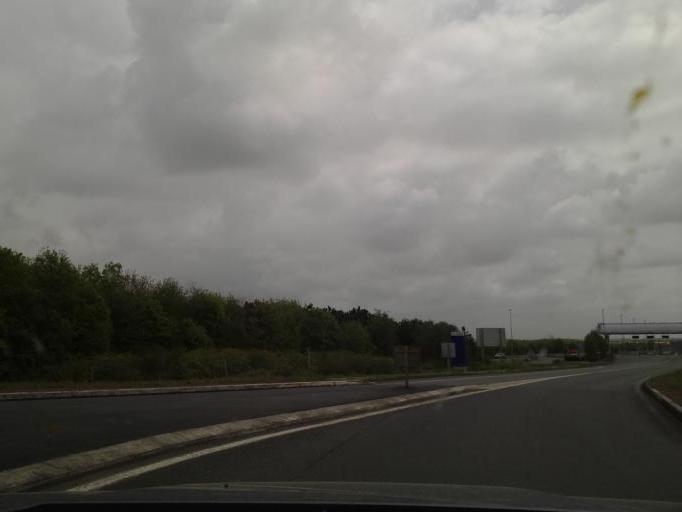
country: FR
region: Pays de la Loire
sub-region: Departement de la Vendee
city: Fontenay-le-Comte
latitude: 46.4374
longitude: -0.8241
